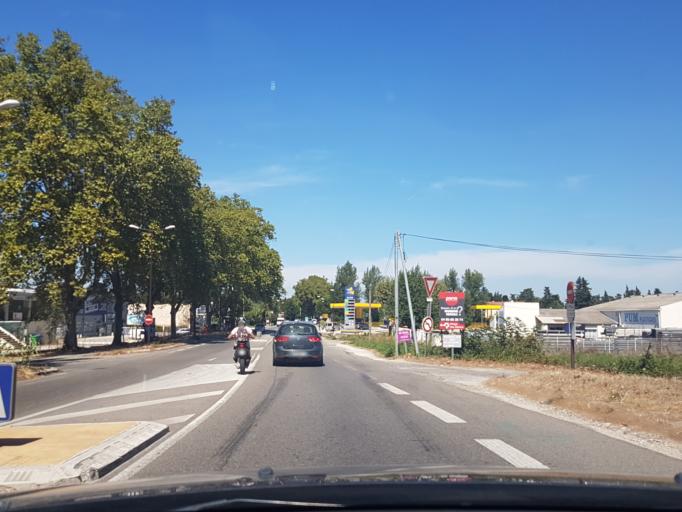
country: FR
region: Provence-Alpes-Cote d'Azur
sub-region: Departement des Bouches-du-Rhone
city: Rognonas
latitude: 43.9174
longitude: 4.8095
